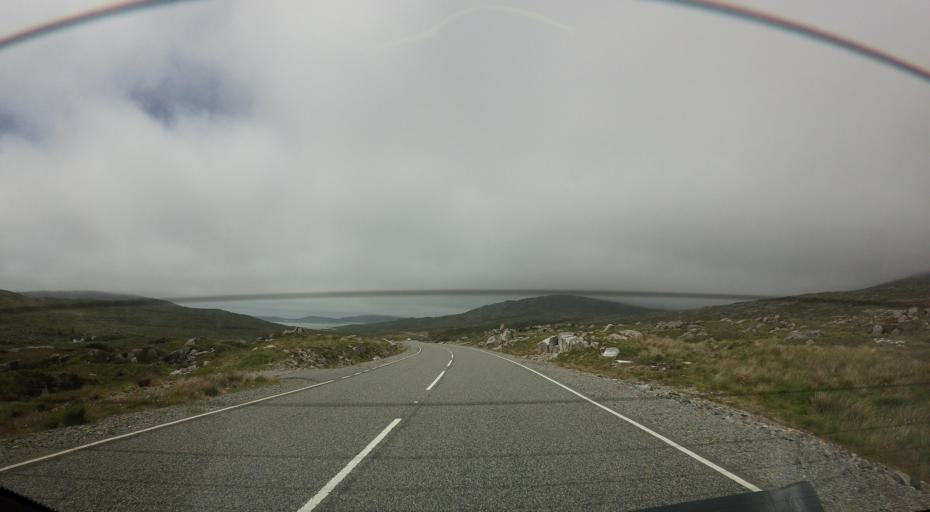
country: GB
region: Scotland
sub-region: Eilean Siar
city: Harris
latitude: 57.8618
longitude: -6.8690
